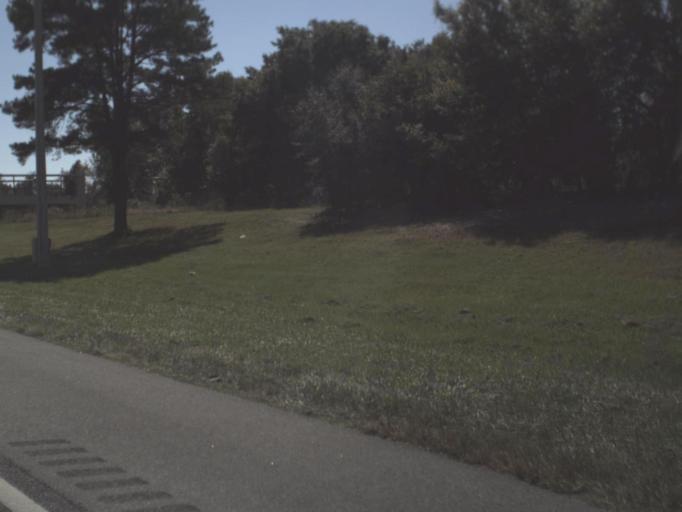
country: US
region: Florida
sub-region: Sumter County
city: Wildwood
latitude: 28.8178
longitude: -82.0184
